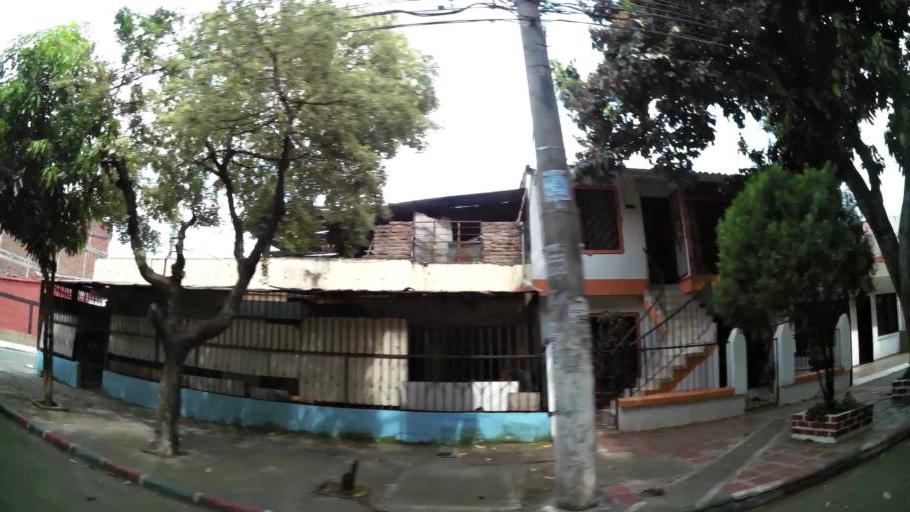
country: CO
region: Valle del Cauca
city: Cali
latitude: 3.4850
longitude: -76.5034
